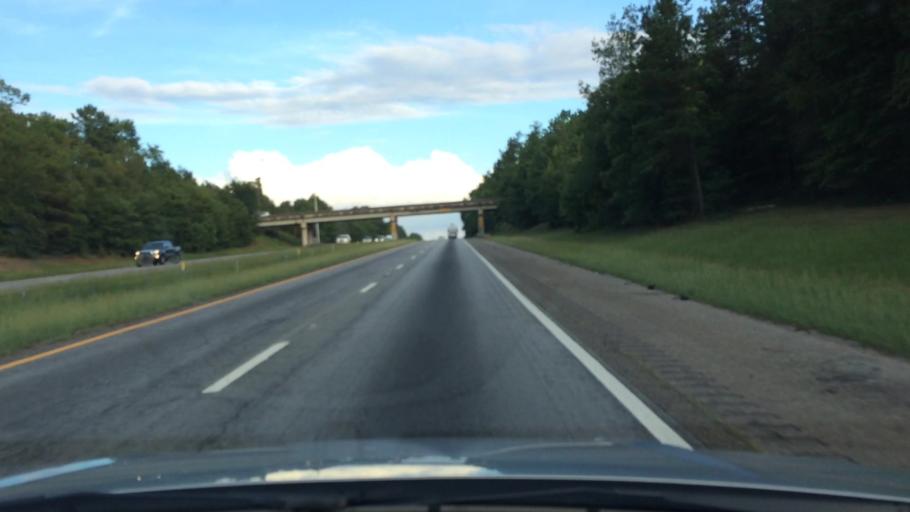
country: US
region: South Carolina
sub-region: Lexington County
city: Irmo
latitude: 34.1235
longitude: -81.2003
